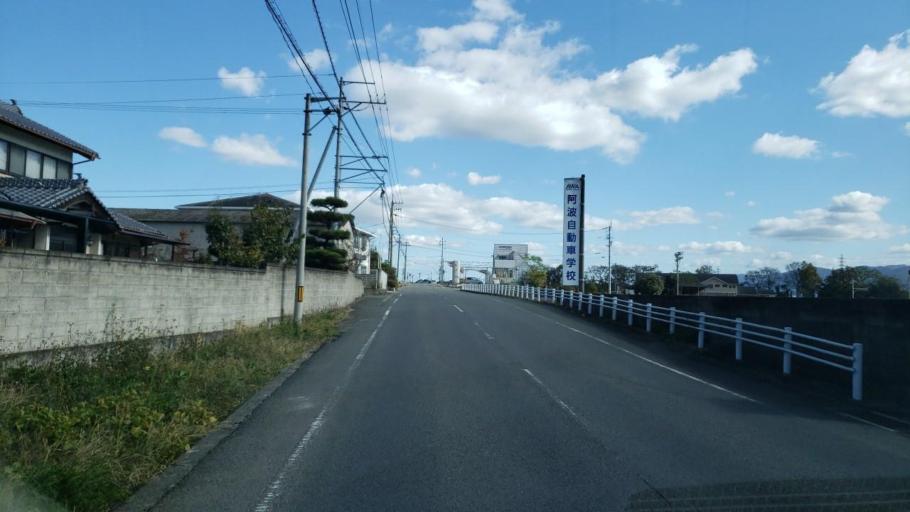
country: JP
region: Tokushima
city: Wakimachi
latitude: 34.0822
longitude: 134.2219
